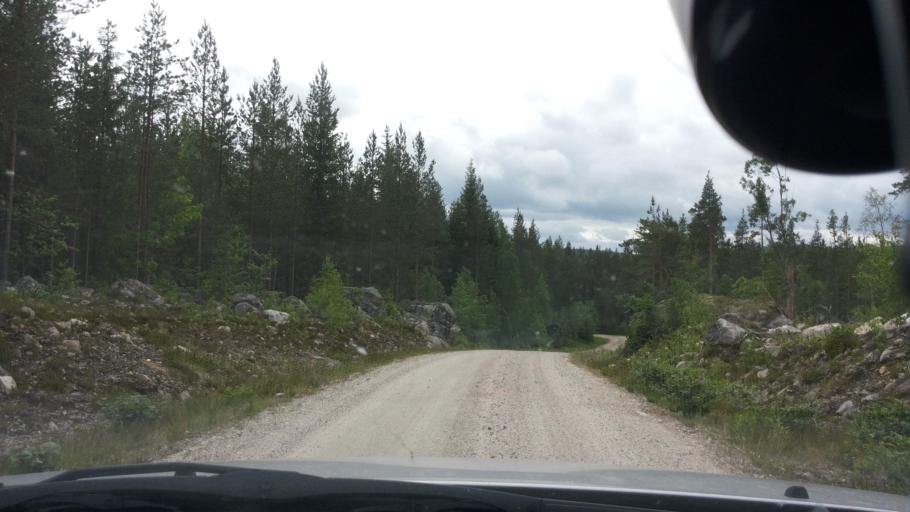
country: SE
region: Gaevleborg
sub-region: Ovanakers Kommun
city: Edsbyn
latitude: 61.4751
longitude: 15.3110
